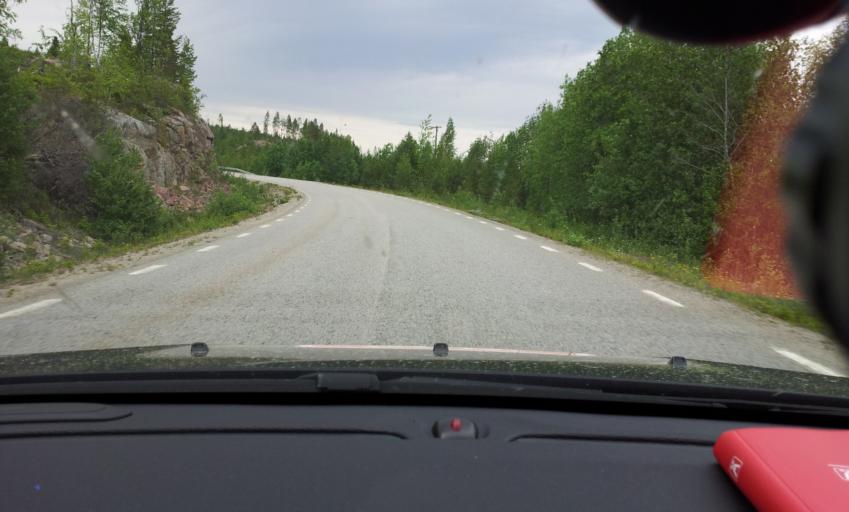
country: SE
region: Jaemtland
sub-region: Bergs Kommun
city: Hoverberg
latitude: 62.6709
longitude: 14.7206
